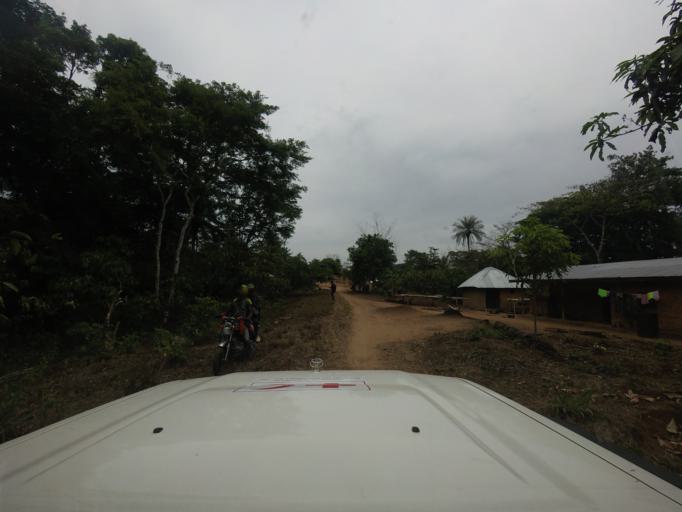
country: SL
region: Eastern Province
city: Buedu
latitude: 8.2438
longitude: -10.2922
